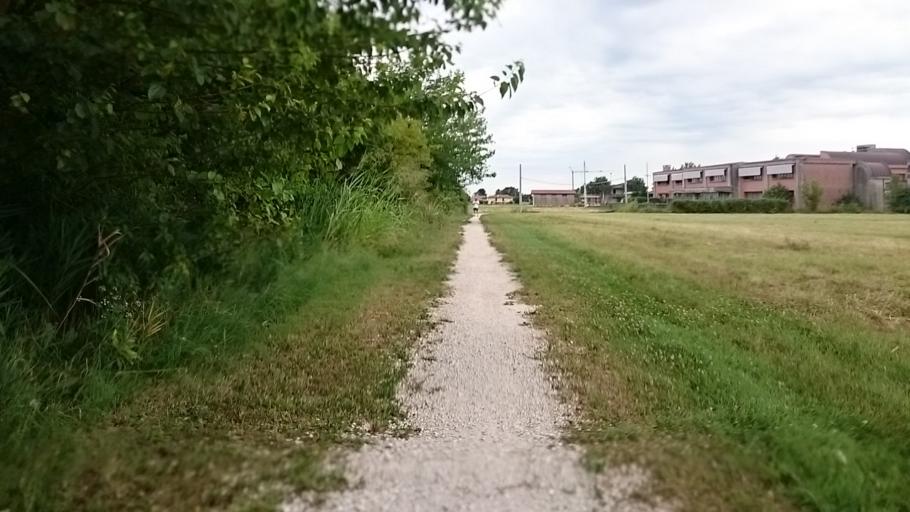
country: IT
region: Veneto
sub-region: Provincia di Padova
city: Albignasego
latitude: 45.3466
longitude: 11.8756
